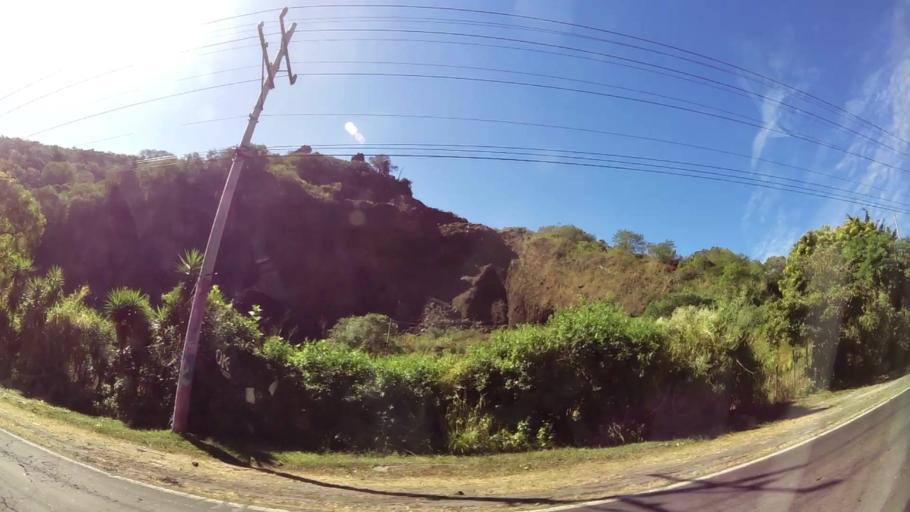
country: SV
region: Sonsonate
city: Juayua
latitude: 13.8541
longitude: -89.7749
